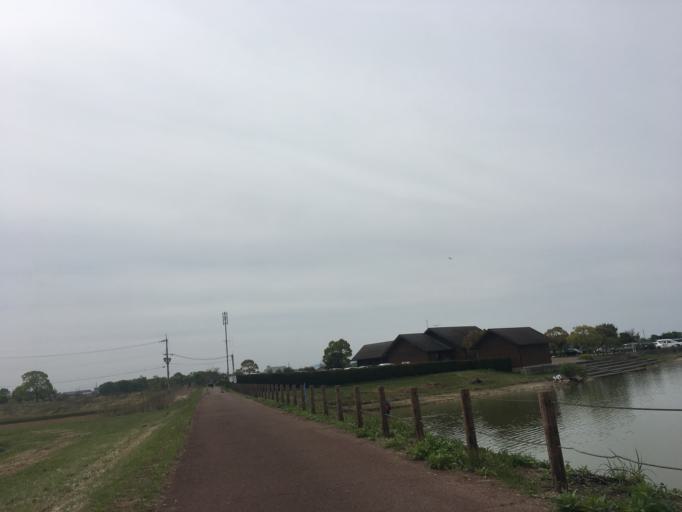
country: JP
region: Hyogo
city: Miki
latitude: 34.7679
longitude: 134.9251
